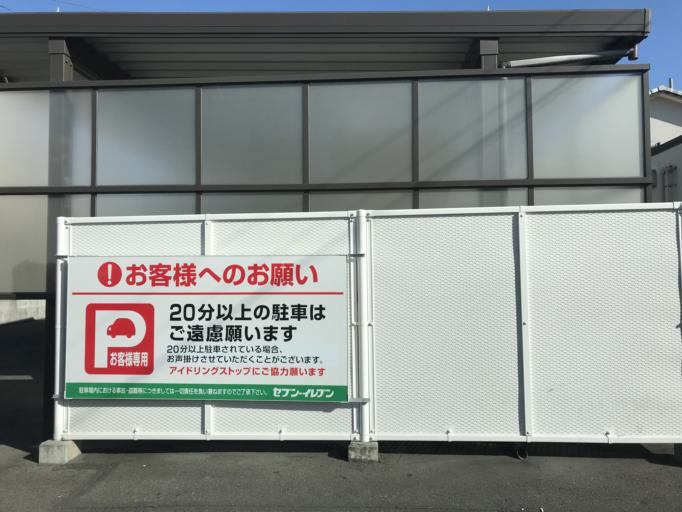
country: JP
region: Aichi
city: Nagoya-shi
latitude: 35.1970
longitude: 136.8472
